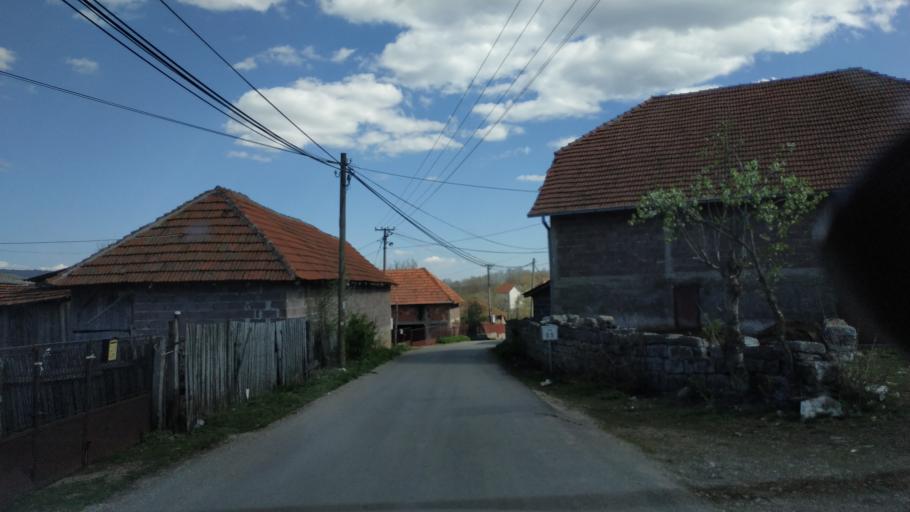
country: RS
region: Central Serbia
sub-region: Zajecarski Okrug
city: Soko Banja
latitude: 43.5707
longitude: 21.9016
